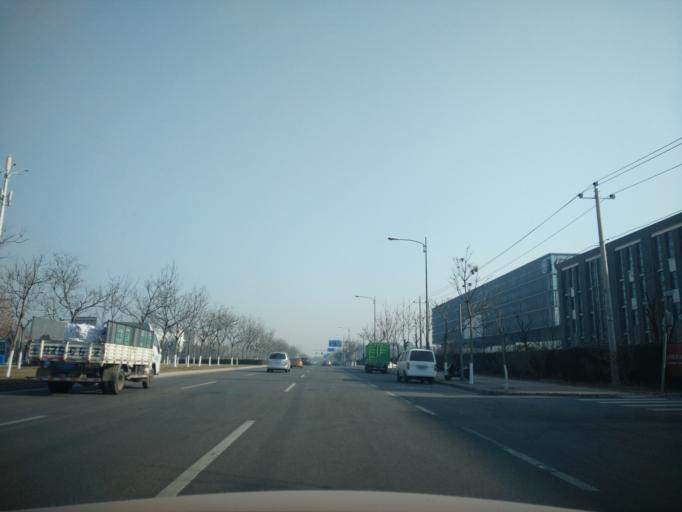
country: CN
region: Beijing
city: Jiugong
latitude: 39.7833
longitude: 116.5220
